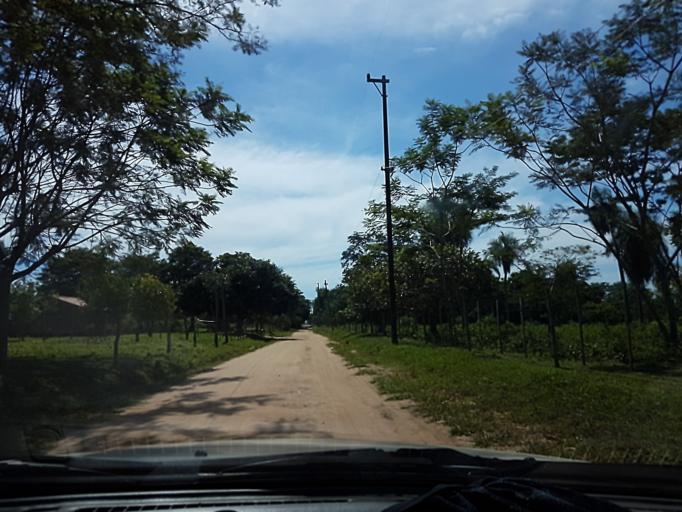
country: PY
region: Cordillera
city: Arroyos y Esteros
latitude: -24.9838
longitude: -57.1995
